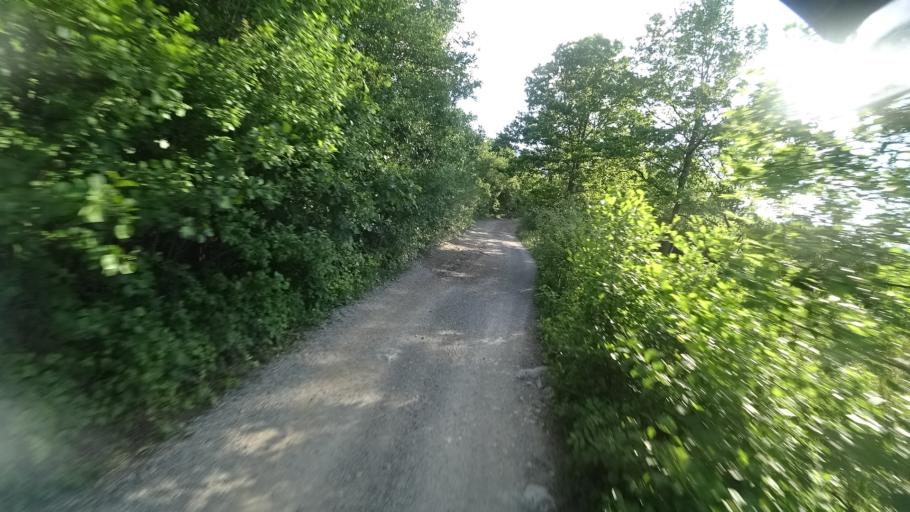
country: HR
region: Licko-Senjska
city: Gospic
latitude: 44.5040
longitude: 15.3120
